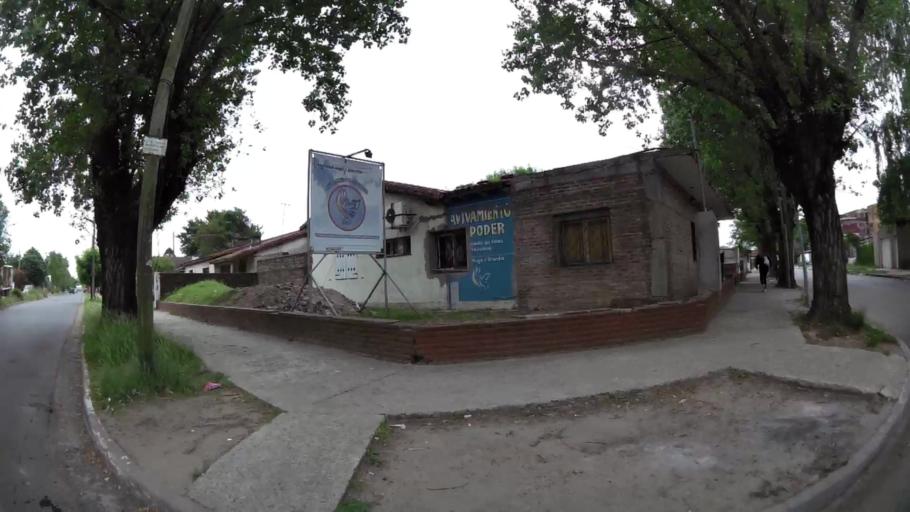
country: AR
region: Buenos Aires
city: San Justo
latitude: -34.7074
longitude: -58.5382
